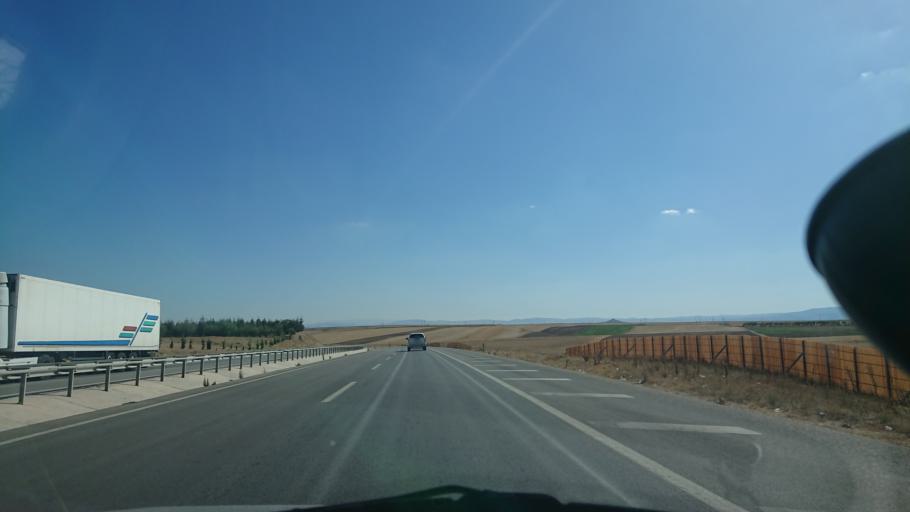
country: TR
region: Eskisehir
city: Mahmudiye
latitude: 39.5060
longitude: 30.9656
